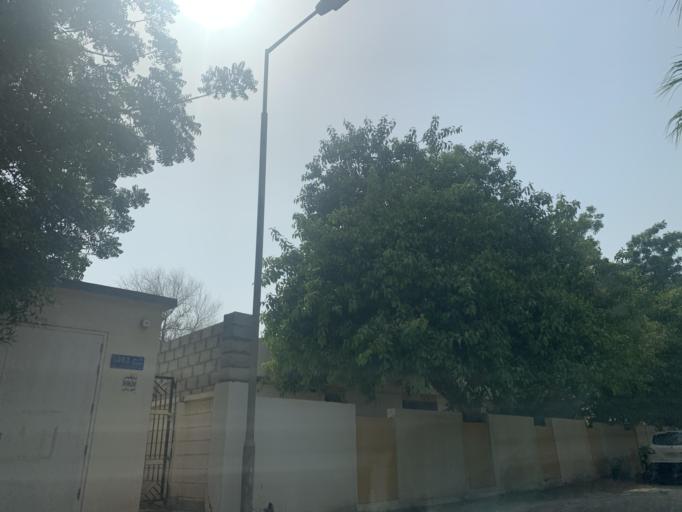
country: BH
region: Manama
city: Jidd Hafs
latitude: 26.1984
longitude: 50.4800
